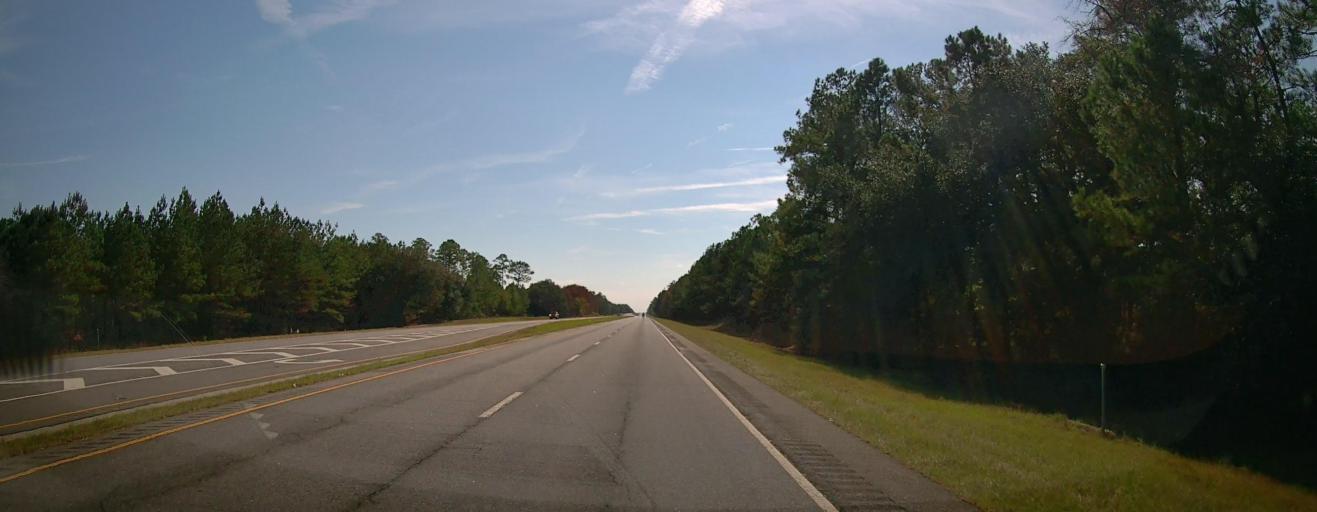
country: US
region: Georgia
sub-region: Lee County
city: Leesburg
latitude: 31.7062
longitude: -83.9906
